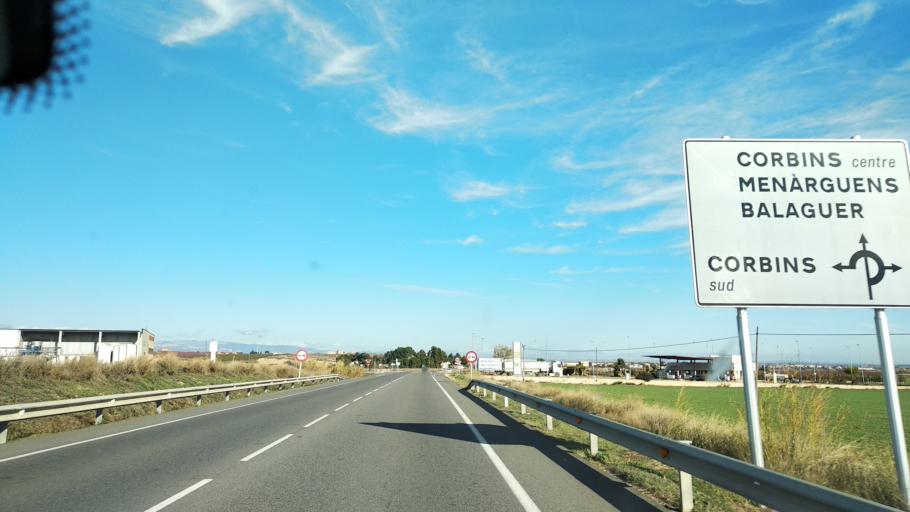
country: ES
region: Catalonia
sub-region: Provincia de Lleida
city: Corbins
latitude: 41.6795
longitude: 0.6792
